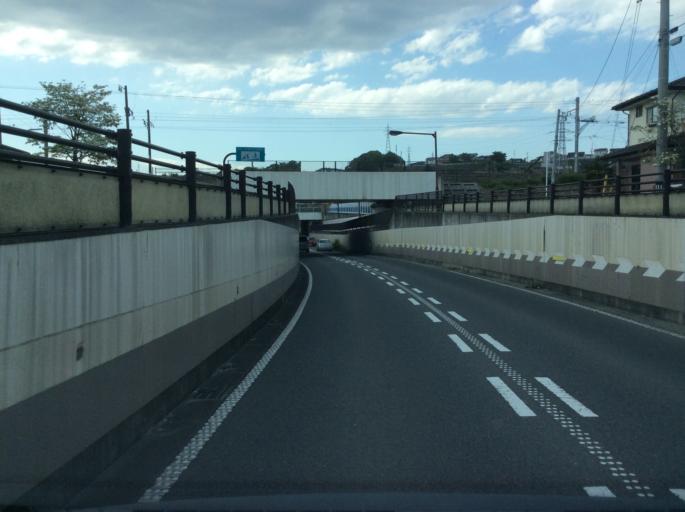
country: JP
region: Fukushima
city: Iwaki
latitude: 36.9570
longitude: 140.8601
